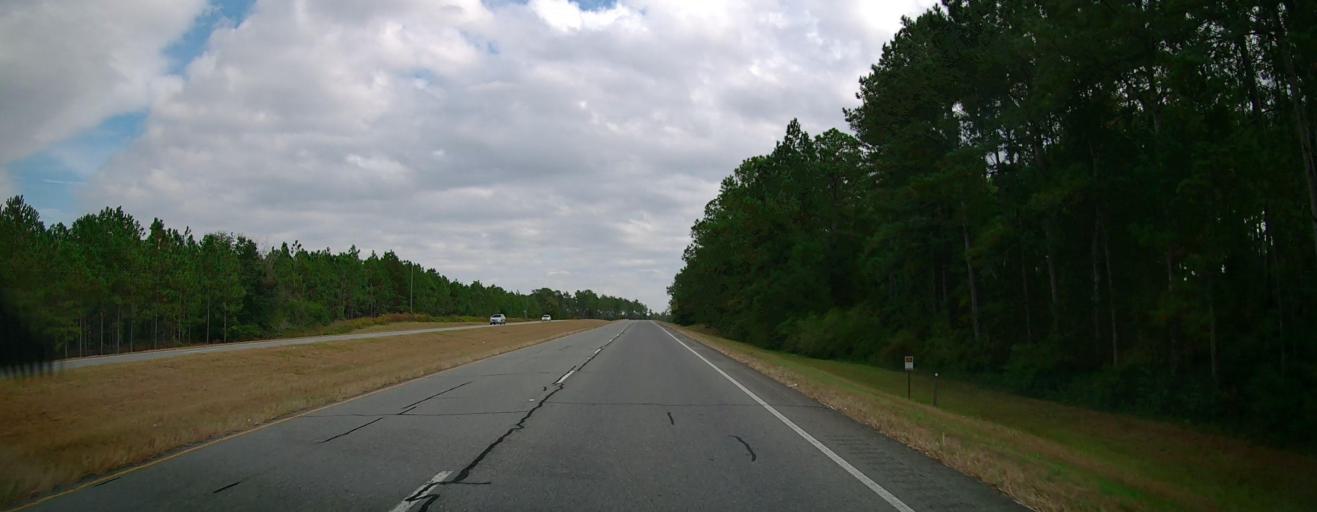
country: US
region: Georgia
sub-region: Thomas County
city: Meigs
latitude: 31.1009
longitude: -84.1036
